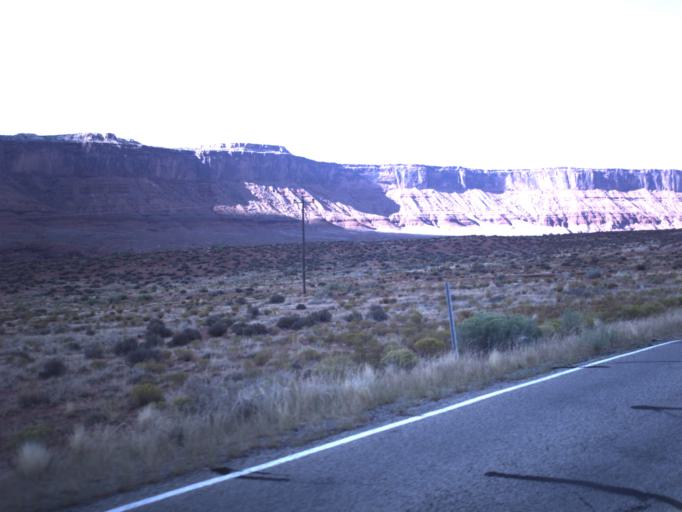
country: US
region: Utah
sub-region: Grand County
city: Moab
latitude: 38.7154
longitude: -109.3700
